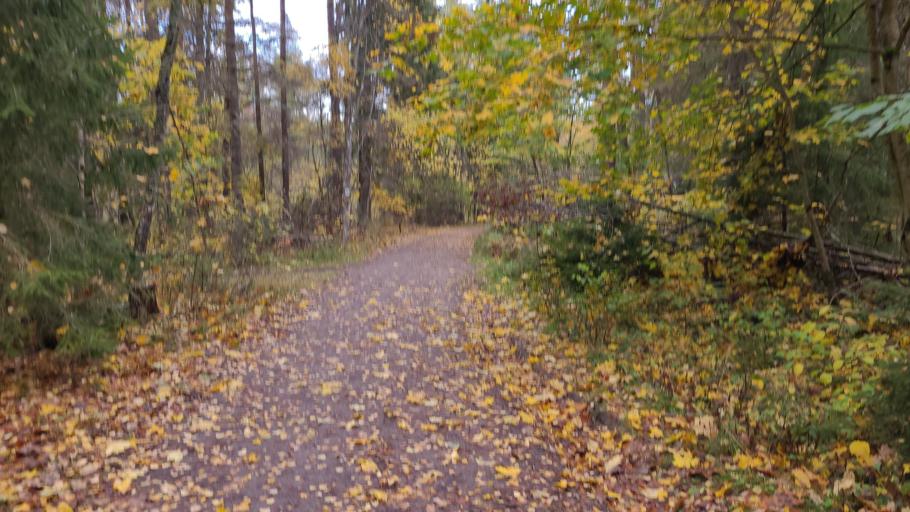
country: SE
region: Stockholm
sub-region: Solna Kommun
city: Rasunda
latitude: 59.3906
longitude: 17.9741
